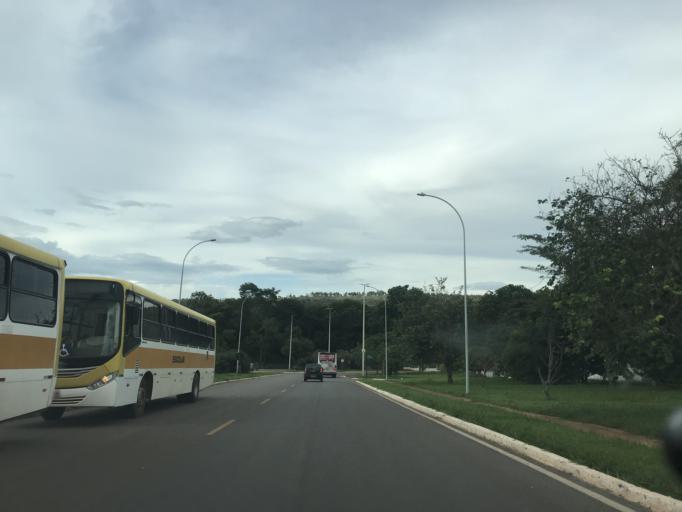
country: BR
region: Federal District
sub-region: Brasilia
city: Brasilia
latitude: -15.6400
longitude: -47.8017
